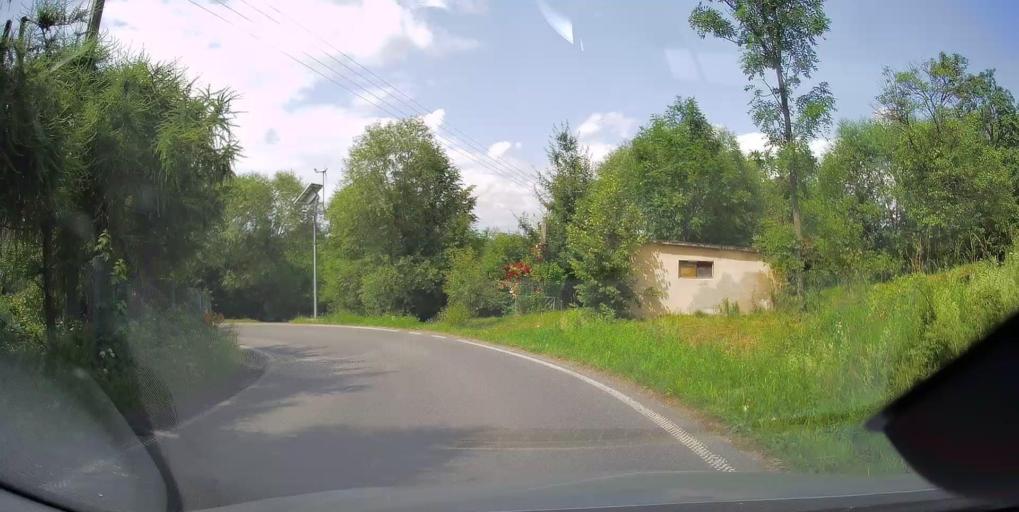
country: PL
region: Lesser Poland Voivodeship
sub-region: Powiat nowosadecki
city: Korzenna
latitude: 49.7043
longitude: 20.7631
